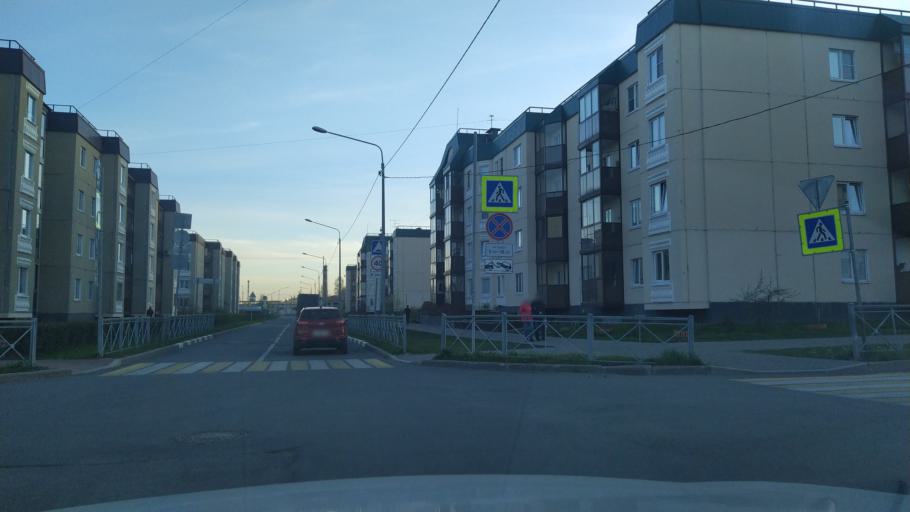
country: RU
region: St.-Petersburg
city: Pushkin
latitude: 59.7050
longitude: 30.3799
